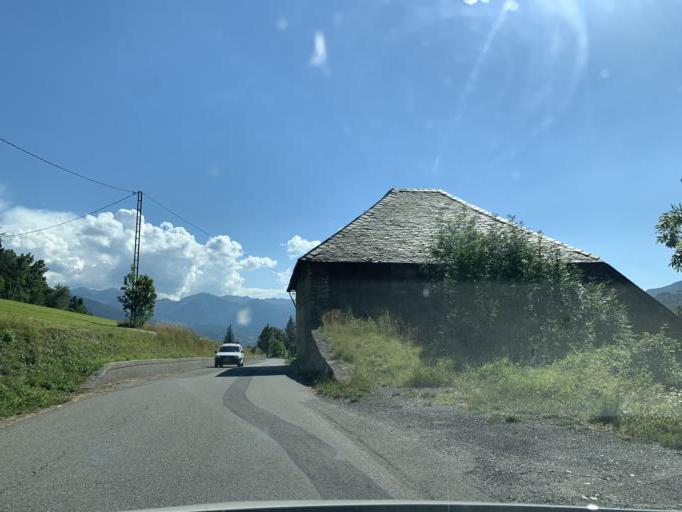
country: FR
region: Provence-Alpes-Cote d'Azur
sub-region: Departement des Hautes-Alpes
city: Embrun
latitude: 44.5795
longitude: 6.5276
